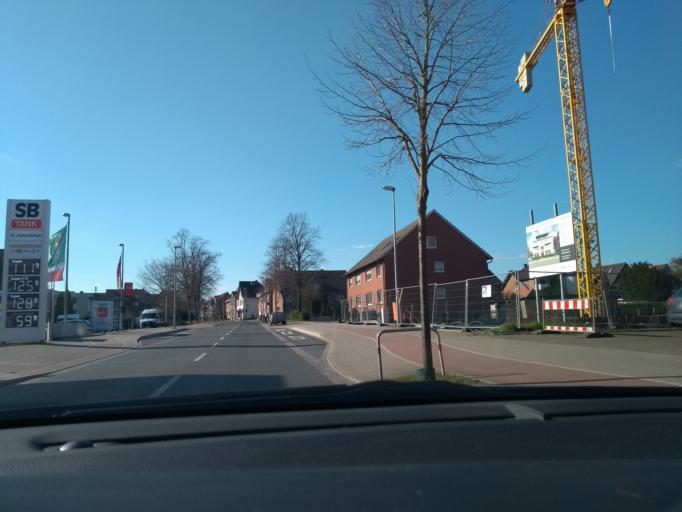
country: DE
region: North Rhine-Westphalia
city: Lunen
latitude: 51.6268
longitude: 7.4958
